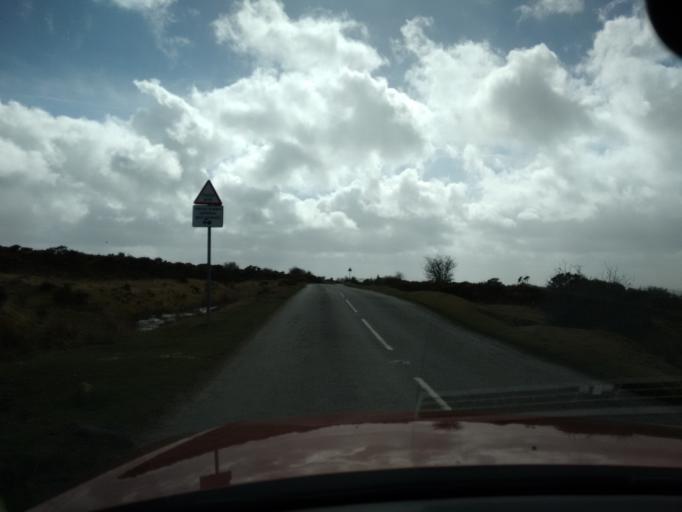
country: GB
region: England
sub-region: Cornwall
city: Liskeard
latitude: 50.5053
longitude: -4.4678
